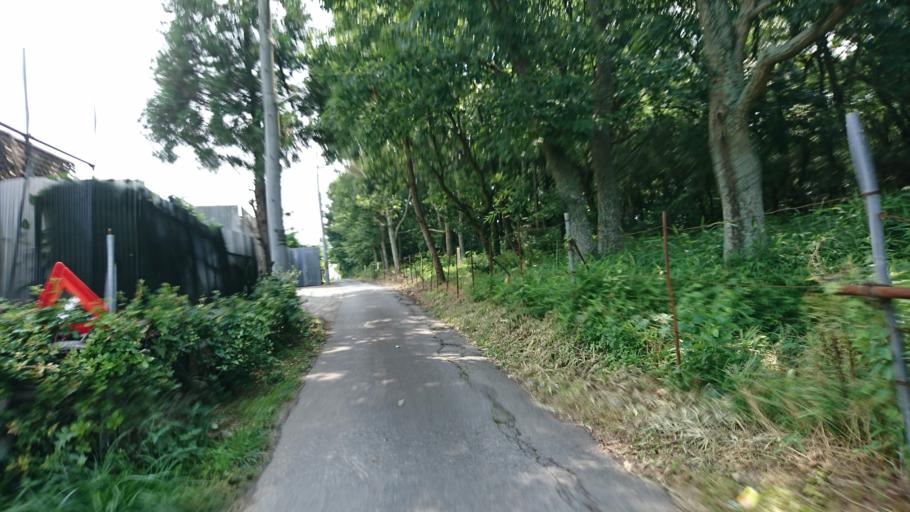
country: JP
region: Hyogo
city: Miki
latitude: 34.7533
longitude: 134.9238
